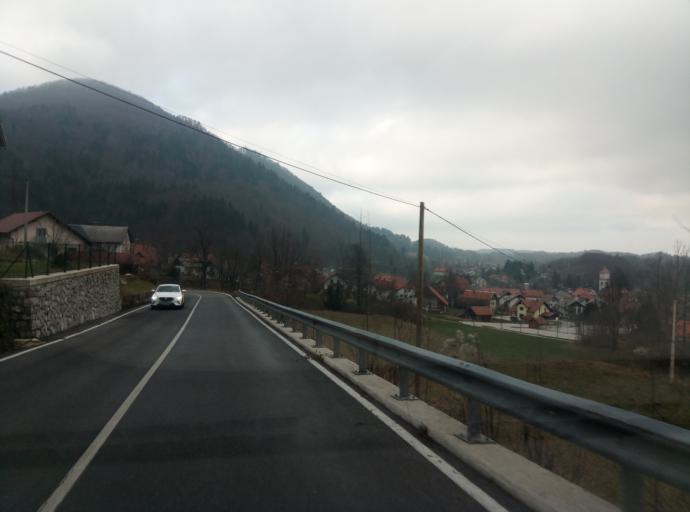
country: SI
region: Idrija
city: Idrija
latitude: 45.9227
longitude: 14.0463
